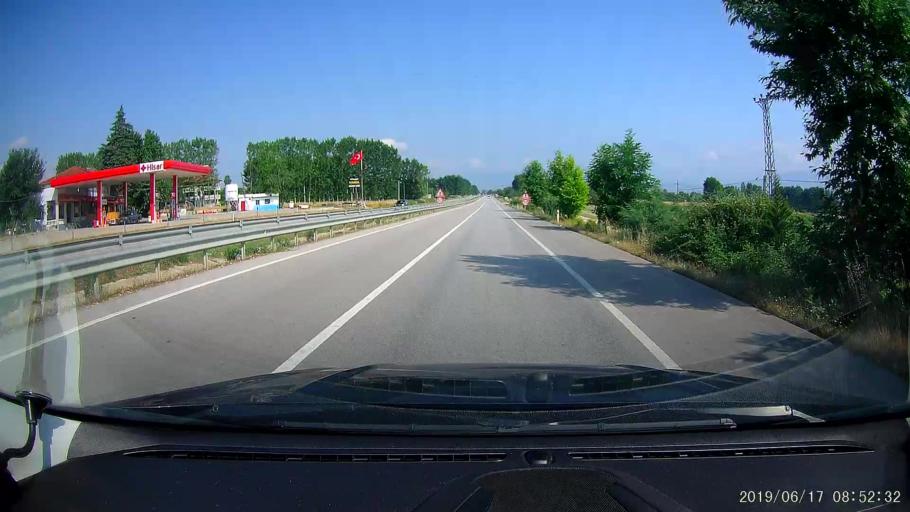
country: TR
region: Tokat
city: Erbaa
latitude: 40.6990
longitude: 36.4951
